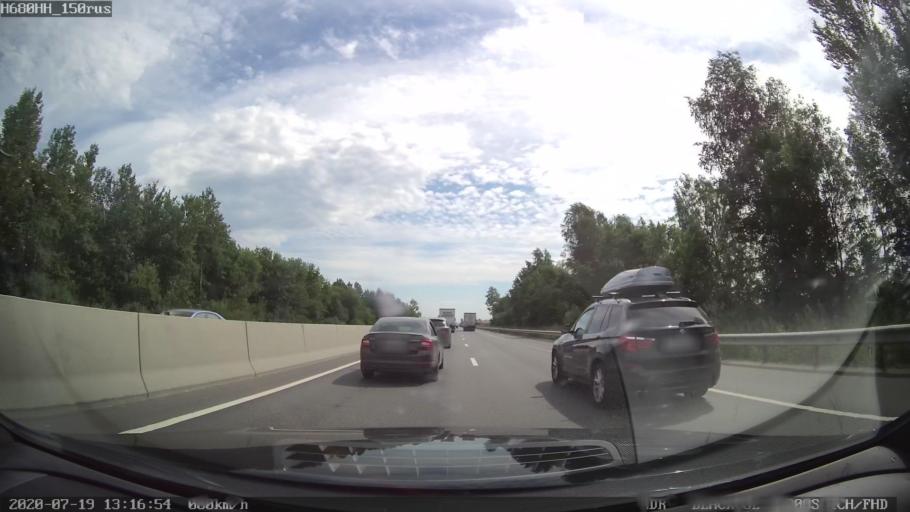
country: RU
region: St.-Petersburg
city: Kolpino
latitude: 59.7134
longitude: 30.5616
